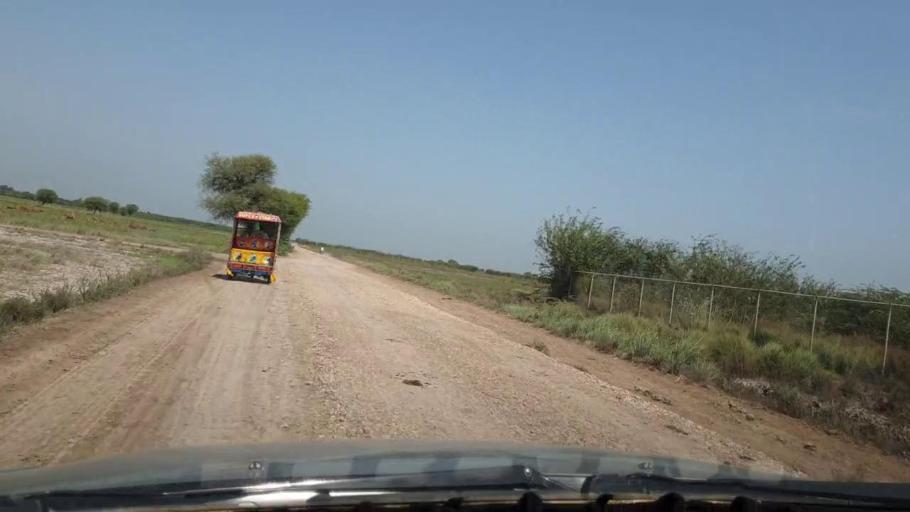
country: PK
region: Sindh
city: Tando Muhammad Khan
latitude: 25.1588
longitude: 68.6337
